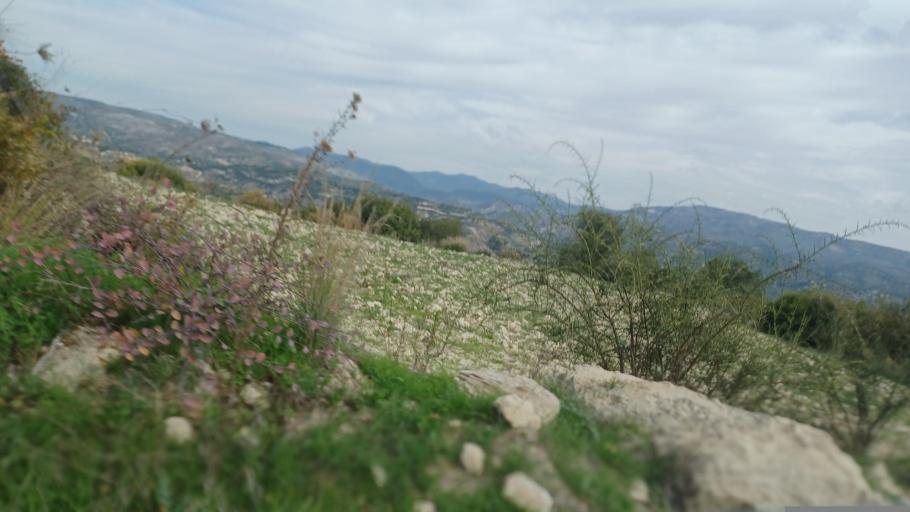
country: CY
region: Pafos
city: Mesogi
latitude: 34.8584
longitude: 32.5221
